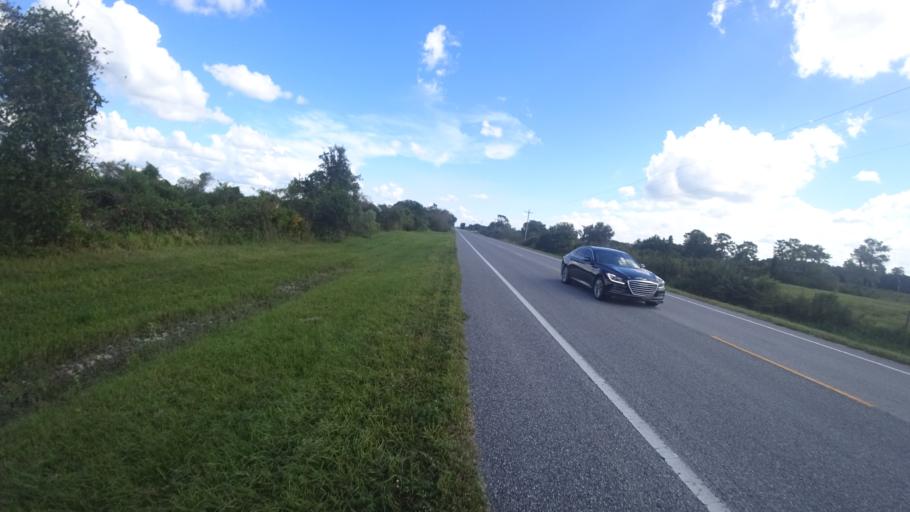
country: US
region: Florida
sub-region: DeSoto County
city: Arcadia
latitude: 27.3105
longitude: -82.1006
